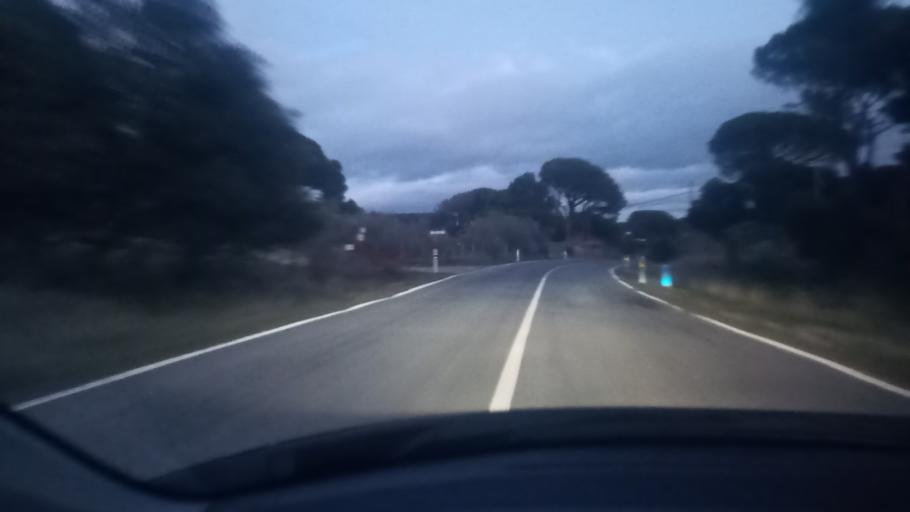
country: ES
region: Madrid
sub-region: Provincia de Madrid
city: Navas del Rey
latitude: 40.4311
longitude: -4.2580
